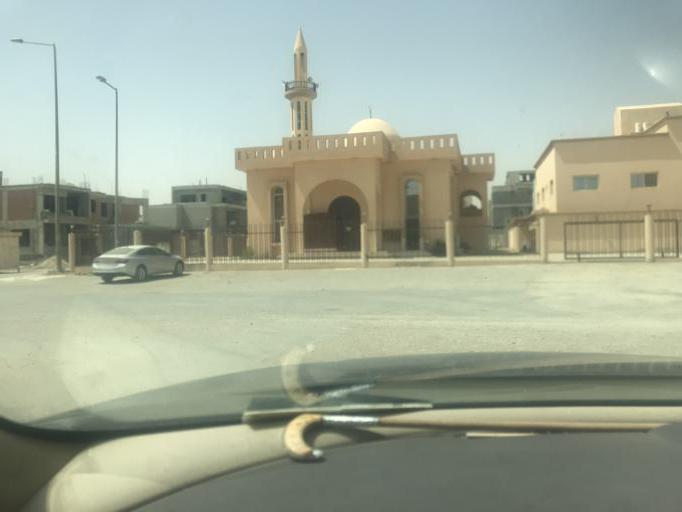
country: SA
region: Ar Riyad
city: Riyadh
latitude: 24.7862
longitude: 46.5846
